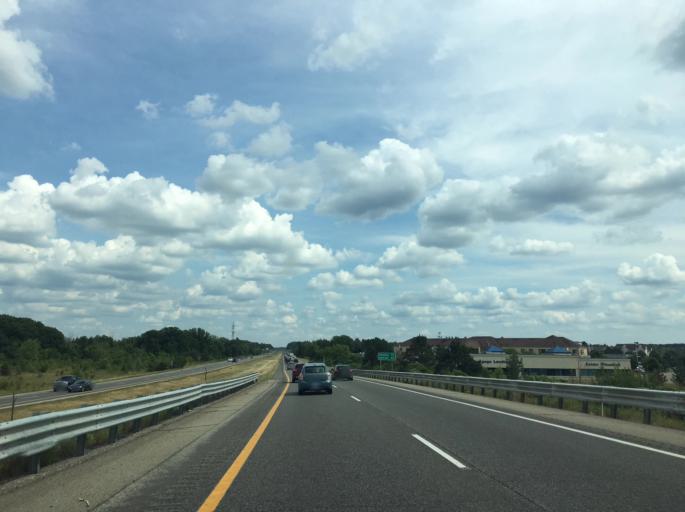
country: US
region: Michigan
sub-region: Genesee County
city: Flint
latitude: 42.9501
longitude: -83.7215
